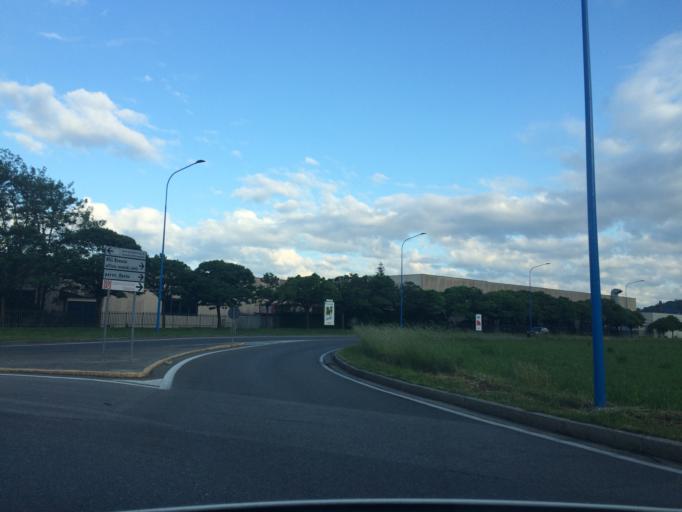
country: IT
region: Lombardy
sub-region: Provincia di Brescia
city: Buffalora-Bettole
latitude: 45.5216
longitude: 10.2632
